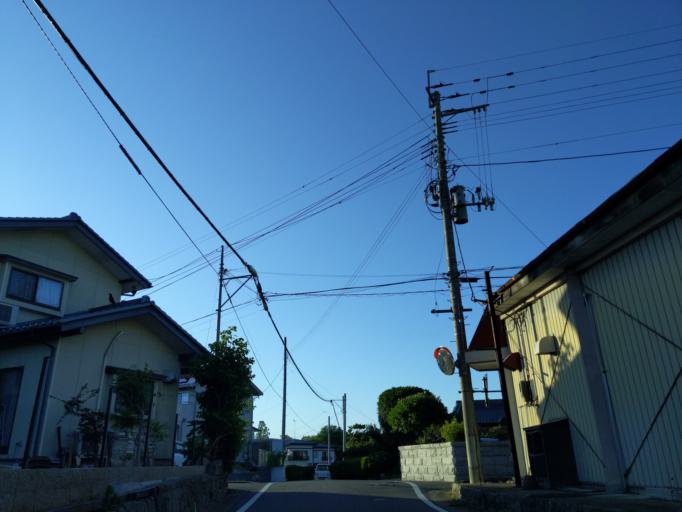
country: JP
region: Fukushima
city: Koriyama
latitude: 37.4212
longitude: 140.4183
